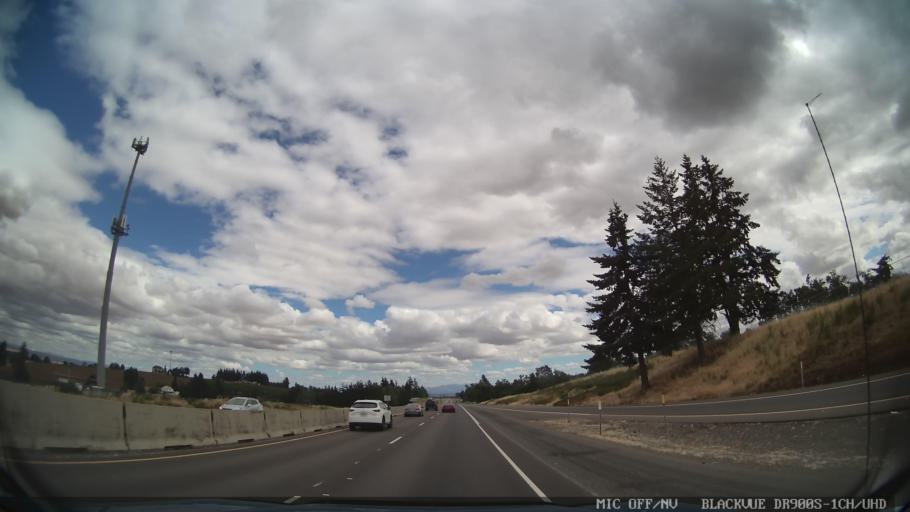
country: US
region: Oregon
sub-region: Marion County
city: Turner
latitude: 44.8840
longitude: -122.9187
